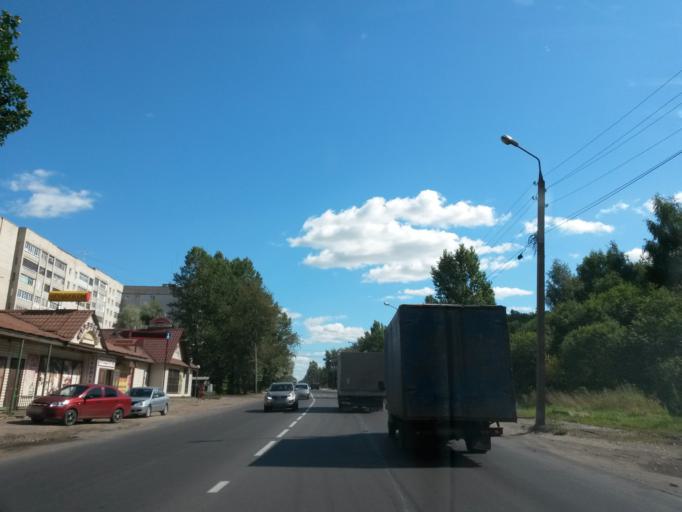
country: RU
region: Jaroslavl
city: Yaroslavl
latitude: 57.5834
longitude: 39.8248
